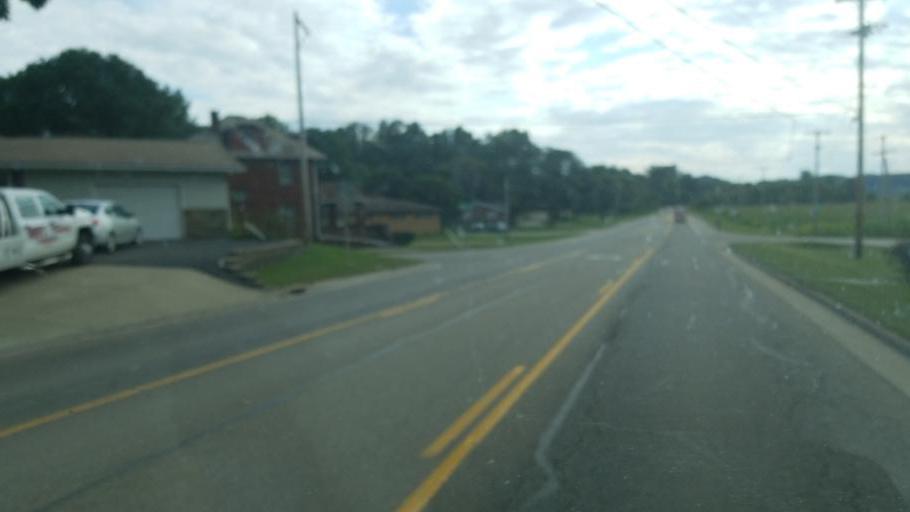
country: US
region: Ohio
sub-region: Tuscarawas County
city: Dover
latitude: 40.5225
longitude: -81.5018
